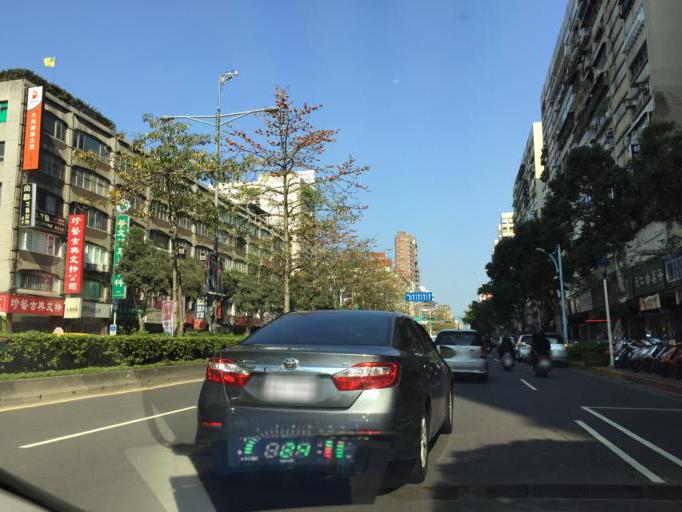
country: TW
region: Taipei
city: Taipei
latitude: 25.0417
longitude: 121.5383
